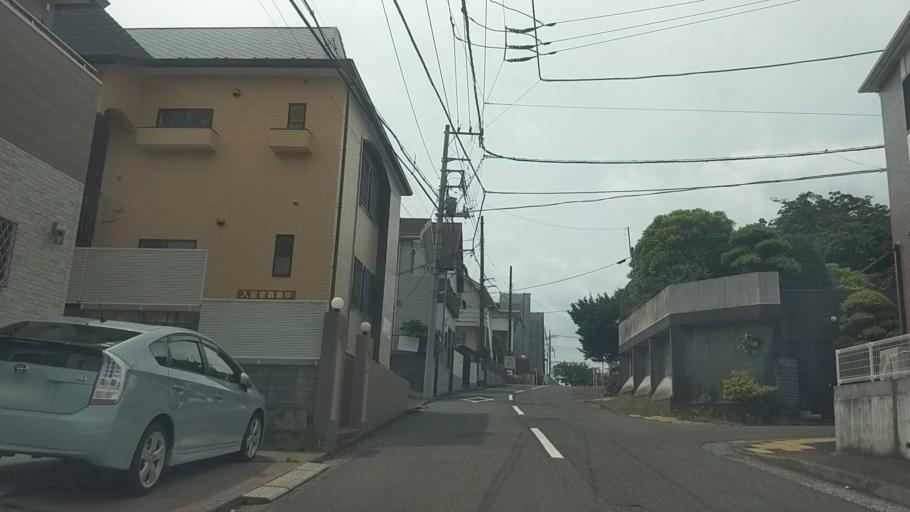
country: JP
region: Kanagawa
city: Fujisawa
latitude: 35.3621
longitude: 139.4723
